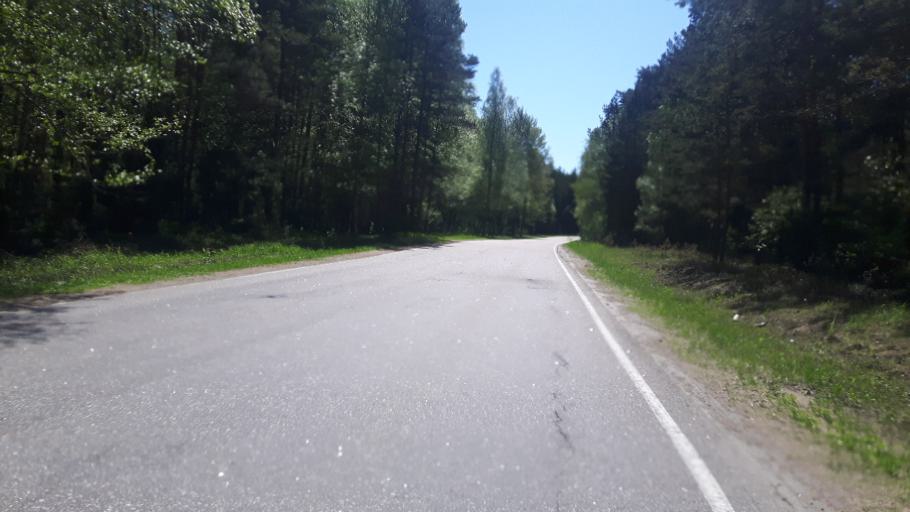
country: RU
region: Leningrad
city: Glebychevo
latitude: 60.3380
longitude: 28.8225
